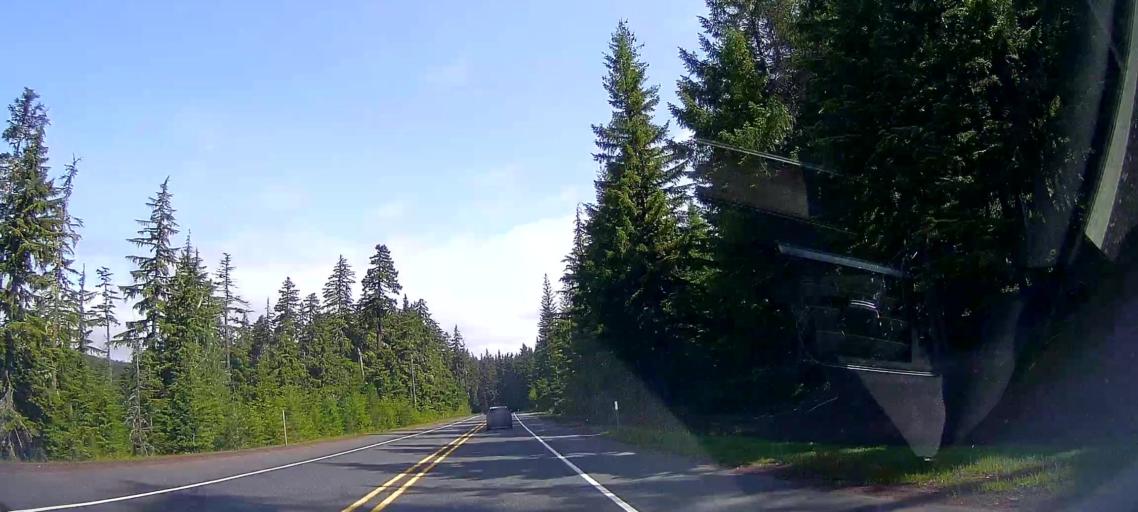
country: US
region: Oregon
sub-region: Clackamas County
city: Mount Hood Village
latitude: 45.1981
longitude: -121.6924
